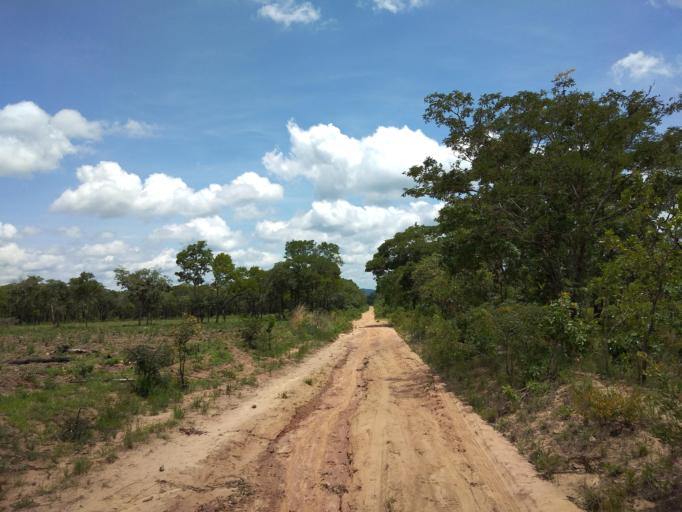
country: ZM
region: Central
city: Mkushi
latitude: -13.9364
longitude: 29.8638
